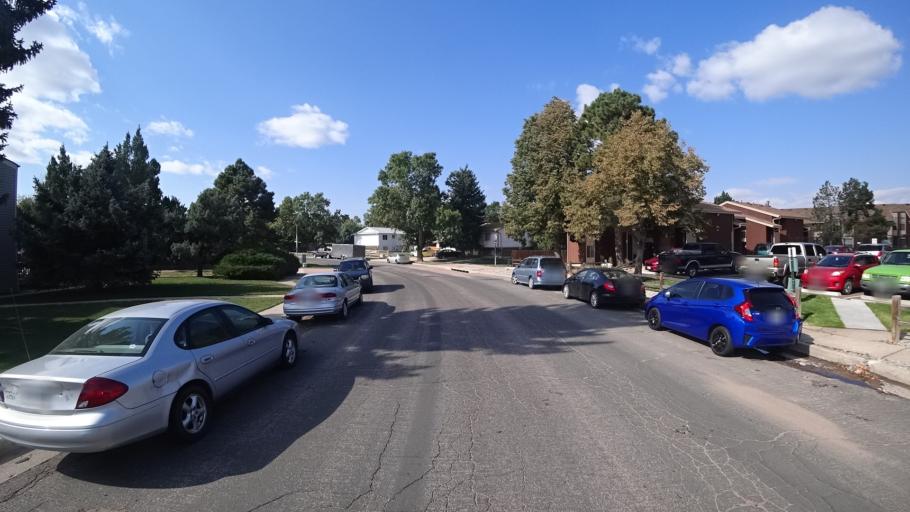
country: US
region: Colorado
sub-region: El Paso County
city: Cimarron Hills
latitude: 38.8855
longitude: -104.7420
